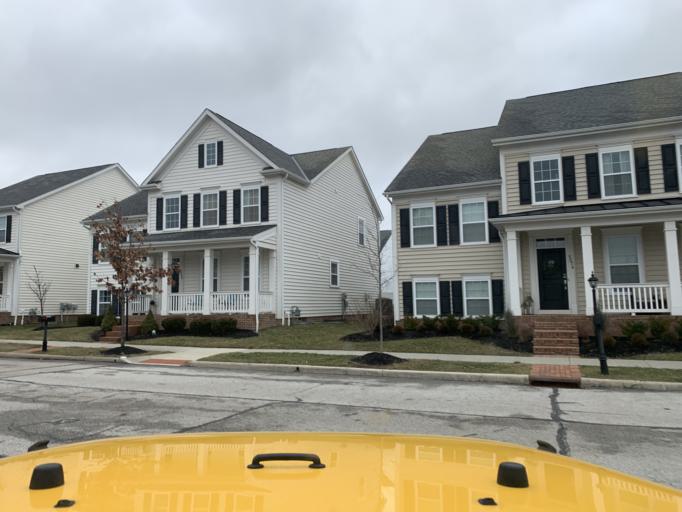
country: US
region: Ohio
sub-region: Franklin County
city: New Albany
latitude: 40.0889
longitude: -82.8056
